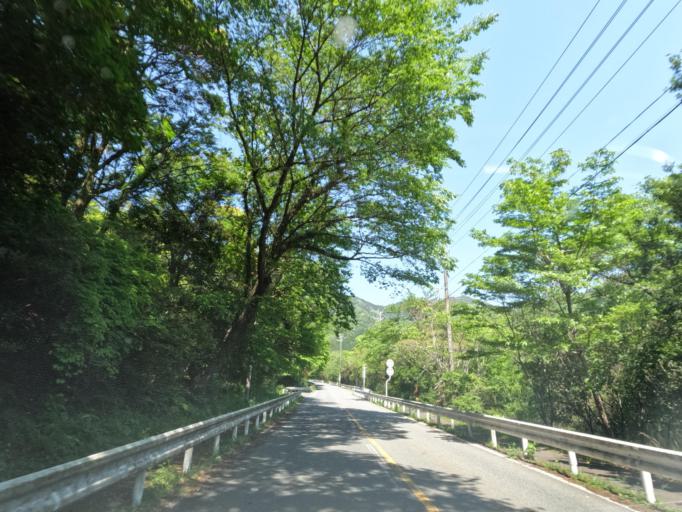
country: JP
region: Mie
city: Komono
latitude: 35.0222
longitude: 136.4640
